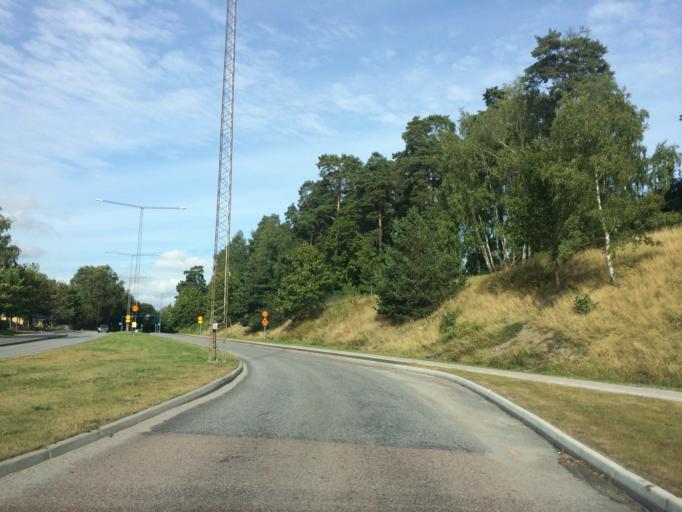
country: SE
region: Stockholm
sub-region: Sollentuna Kommun
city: Sollentuna
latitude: 59.4309
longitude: 17.9509
